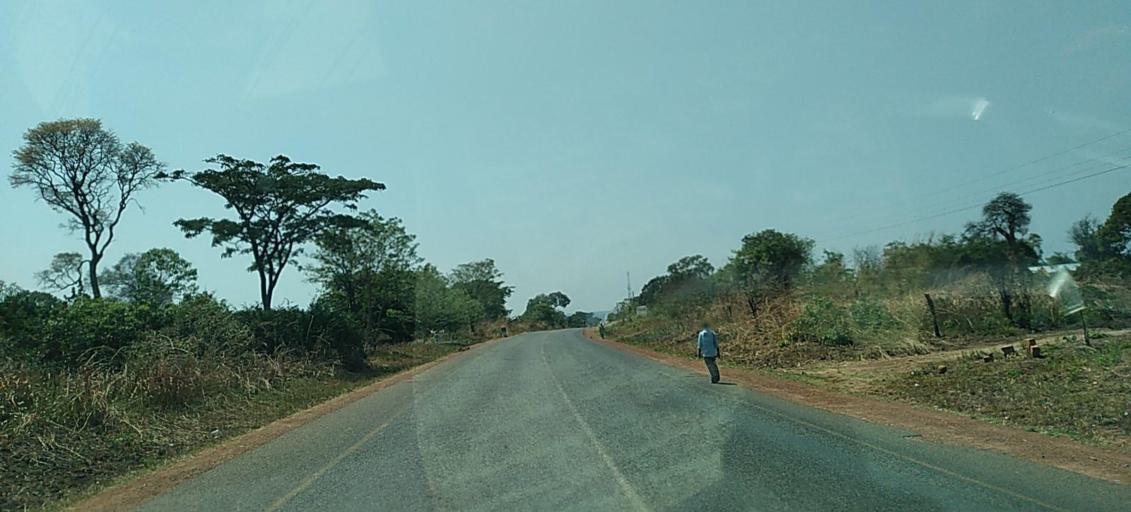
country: ZM
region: North-Western
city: Solwezi
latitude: -12.3229
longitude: 25.8790
